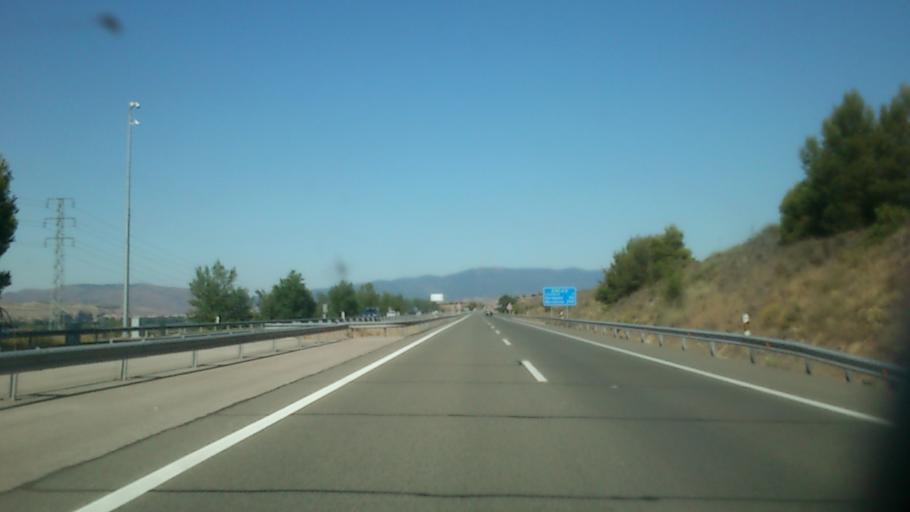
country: ES
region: Aragon
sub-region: Provincia de Zaragoza
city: Terrer
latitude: 41.3167
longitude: -1.6991
